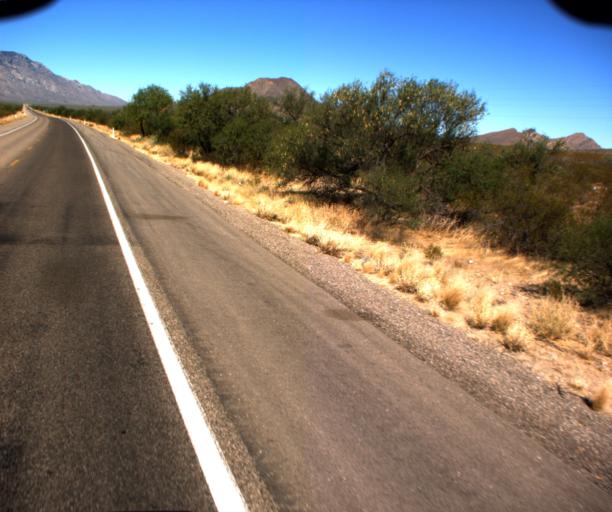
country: US
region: Arizona
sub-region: Pima County
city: Three Points
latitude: 32.0607
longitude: -111.3941
